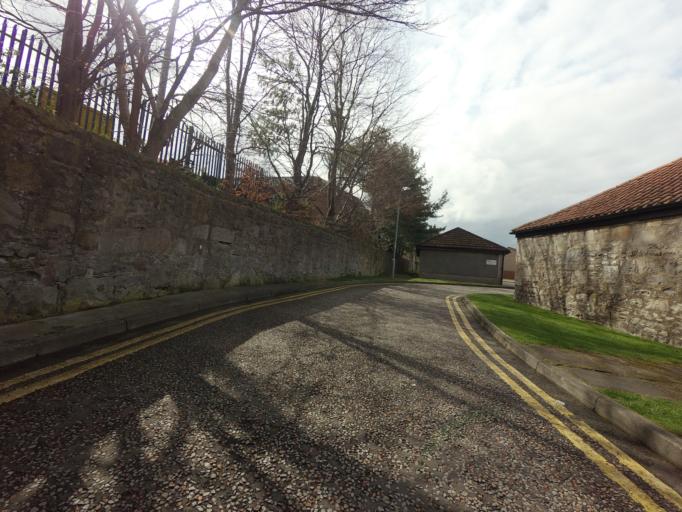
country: GB
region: Scotland
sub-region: Edinburgh
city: Edinburgh
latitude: 55.9708
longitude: -3.1882
